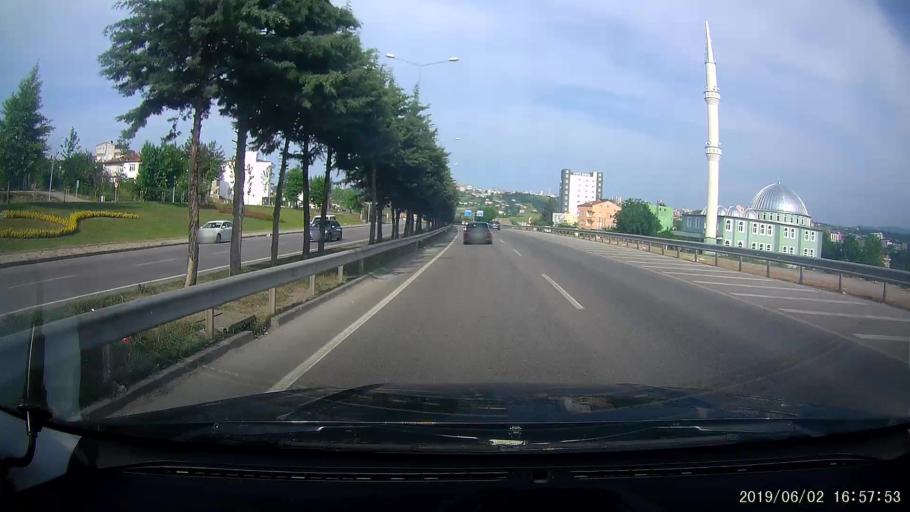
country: TR
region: Samsun
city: Samsun
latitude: 41.2902
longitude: 36.2806
